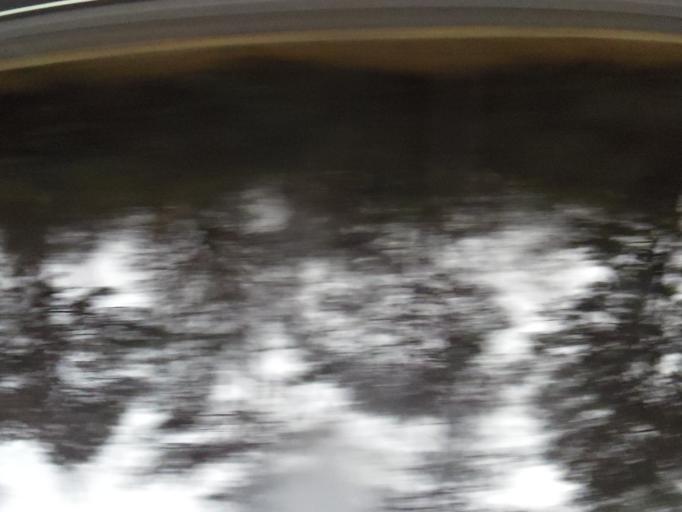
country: US
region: Alabama
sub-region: Cullman County
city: Good Hope
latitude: 34.1494
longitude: -86.8700
